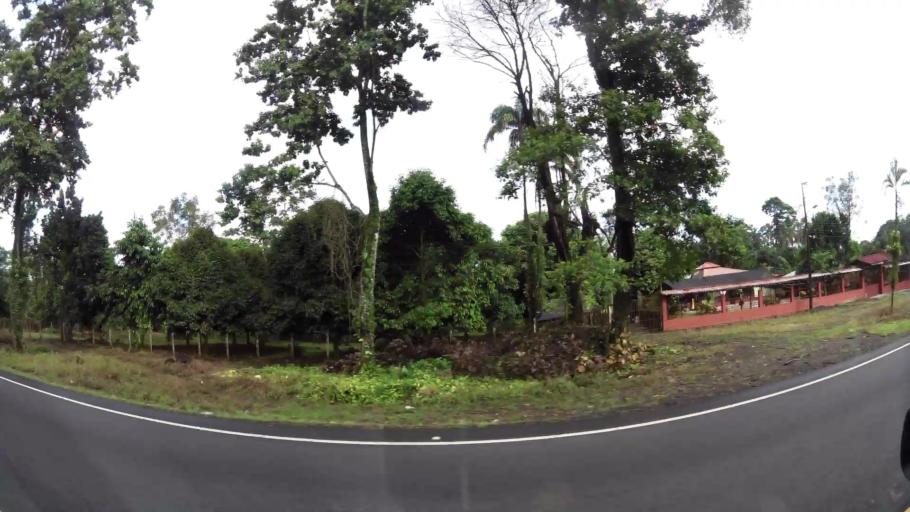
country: CR
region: Limon
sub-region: Canton de Guacimo
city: Guacimo
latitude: 10.2056
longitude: -83.7123
